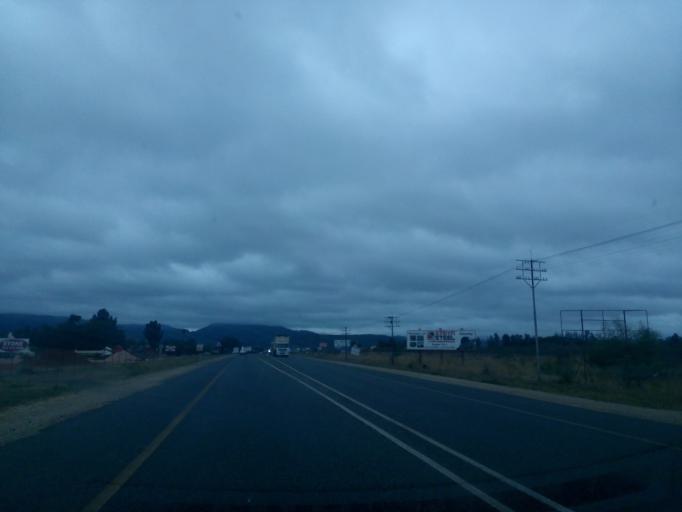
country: ZA
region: Limpopo
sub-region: Vhembe District Municipality
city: Louis Trichardt
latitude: -23.0733
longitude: 29.9103
